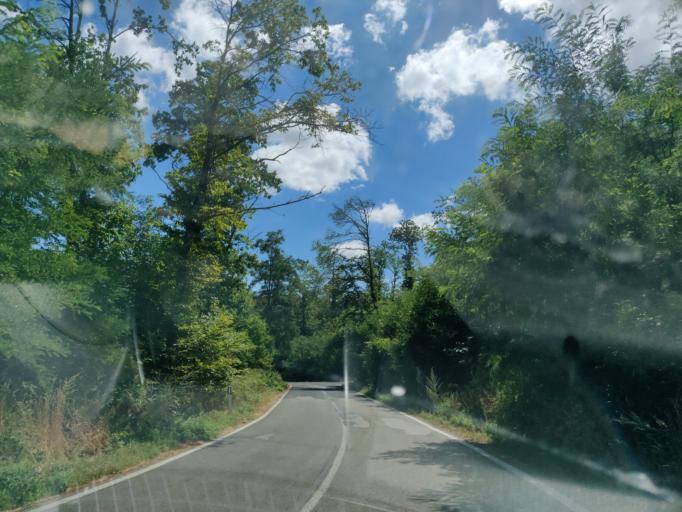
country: IT
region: Tuscany
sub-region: Provincia di Siena
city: Abbadia San Salvatore
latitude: 42.8851
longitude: 11.6570
